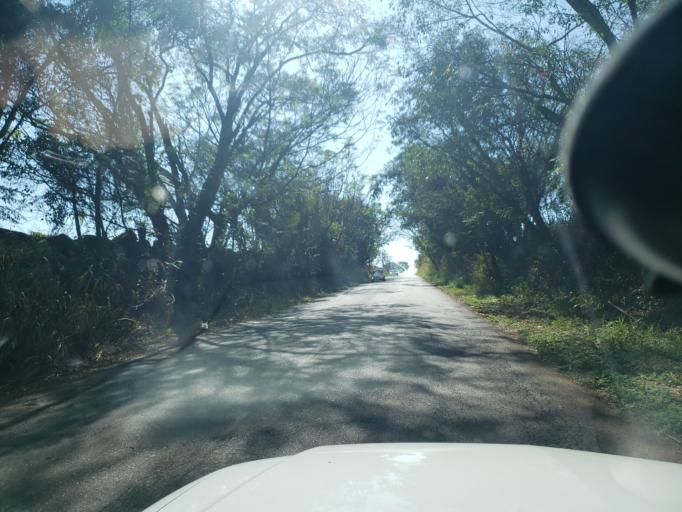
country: BR
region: Sao Paulo
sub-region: Moji-Guacu
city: Mogi-Gaucu
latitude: -22.3425
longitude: -46.8895
